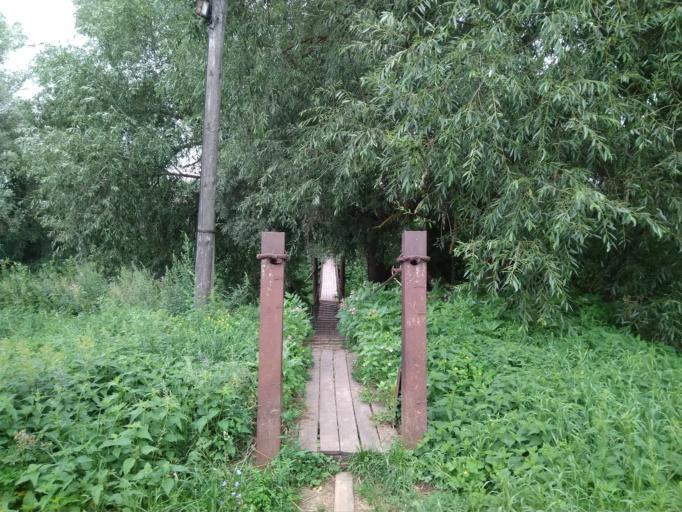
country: RU
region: Mordoviya
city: Ten'gushevo
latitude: 54.7720
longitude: 42.7293
